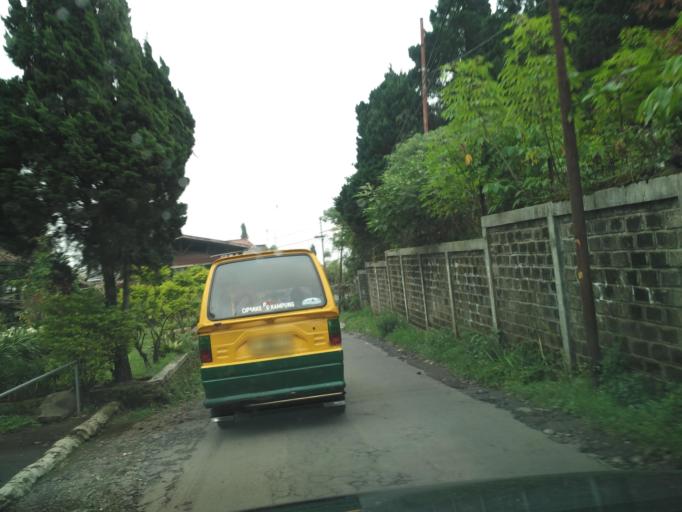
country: ID
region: West Java
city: Sukabumi
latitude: -6.7463
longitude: 107.0378
